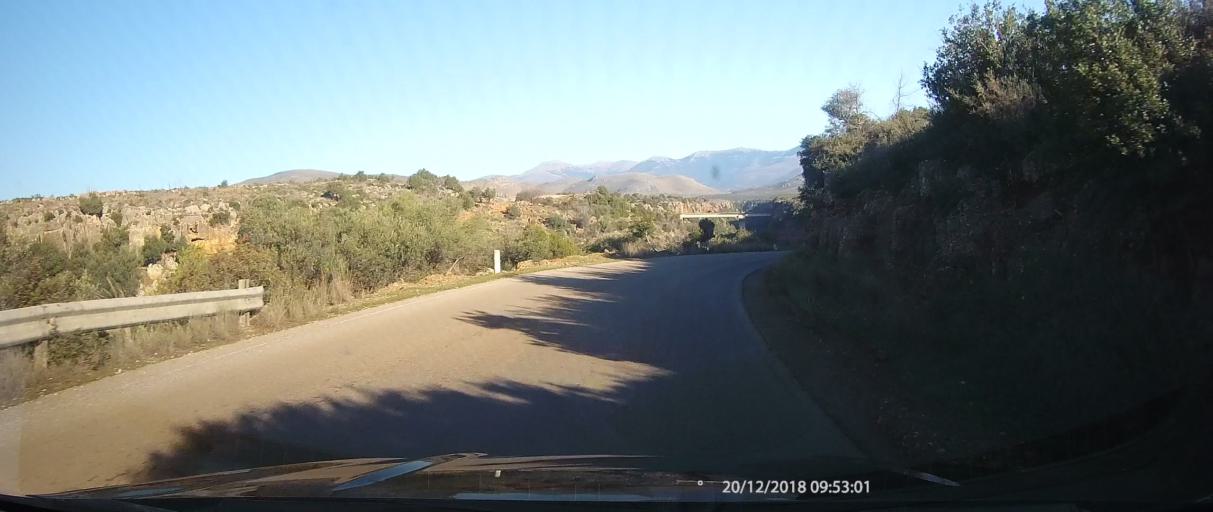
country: GR
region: Peloponnese
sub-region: Nomos Lakonias
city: Yerakion
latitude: 37.0084
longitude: 22.6373
